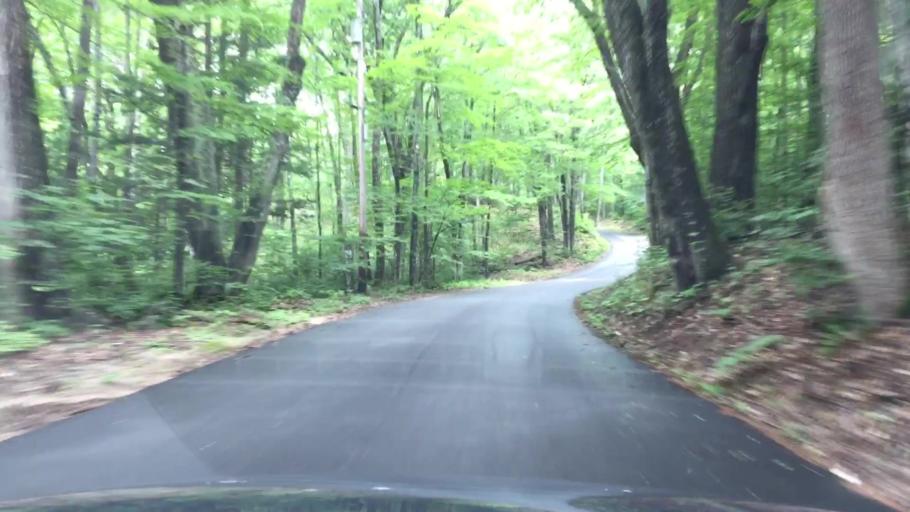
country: US
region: New Hampshire
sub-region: Carroll County
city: Sandwich
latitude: 43.7855
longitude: -71.4702
